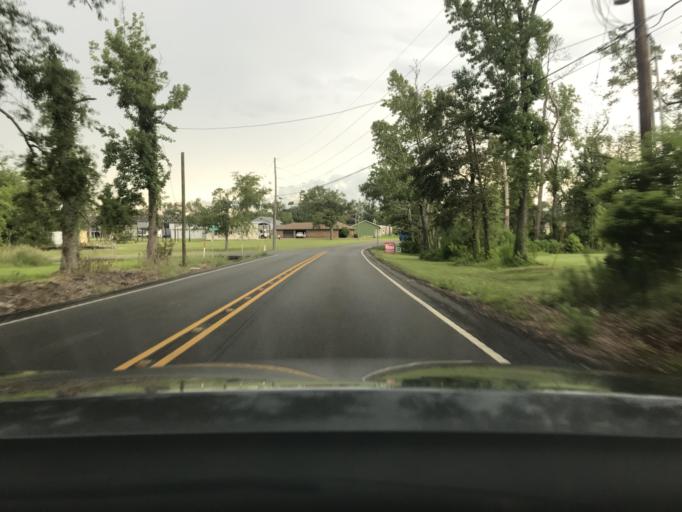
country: US
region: Louisiana
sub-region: Calcasieu Parish
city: Westlake
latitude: 30.2637
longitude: -93.2457
